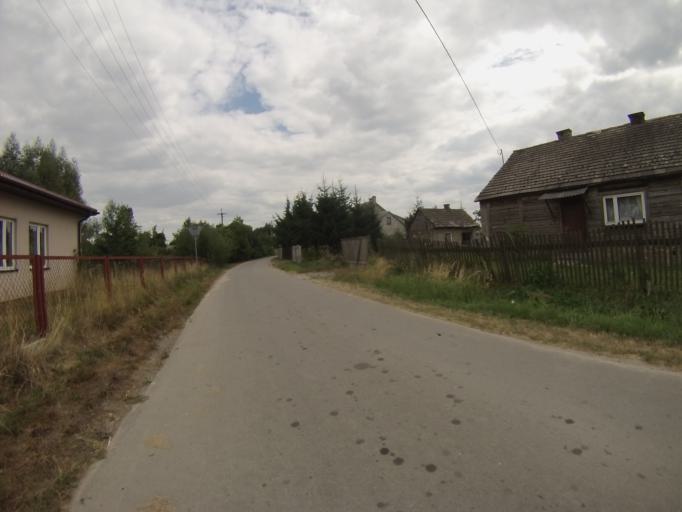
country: PL
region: Swietokrzyskie
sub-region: Powiat staszowski
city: Bogoria
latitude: 50.6868
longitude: 21.2055
